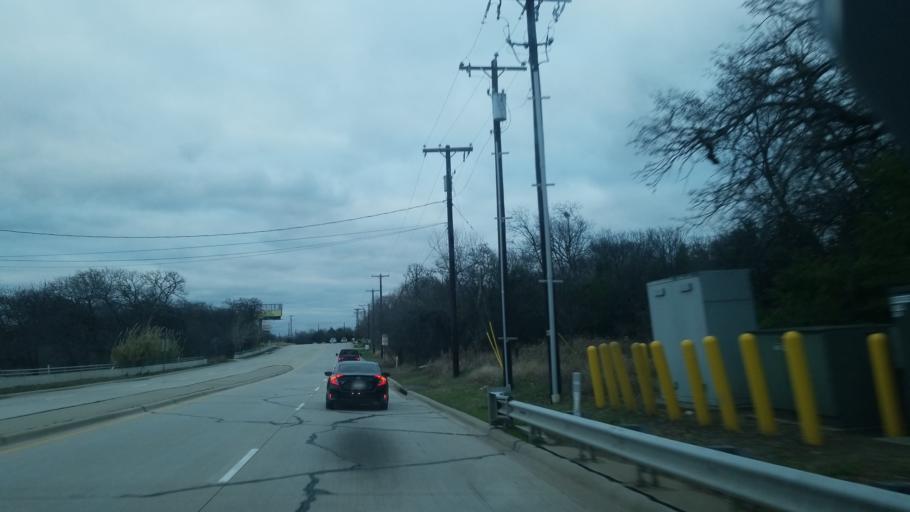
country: US
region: Texas
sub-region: Denton County
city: Lake Dallas
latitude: 33.1404
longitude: -96.9894
